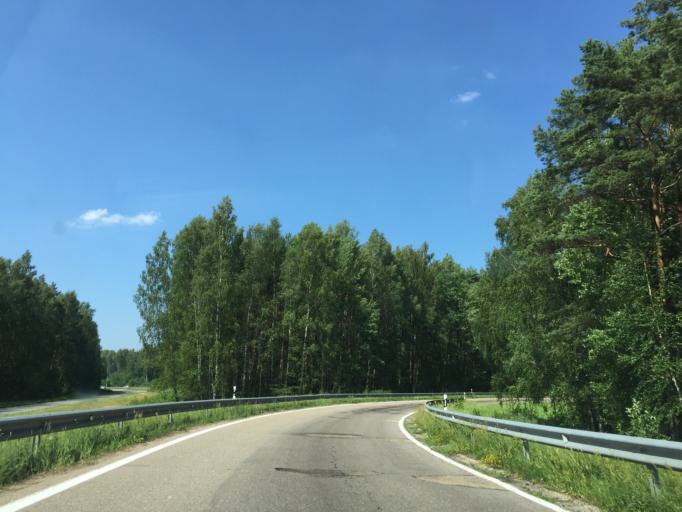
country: LV
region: Babite
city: Pinki
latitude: 56.9522
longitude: 23.9239
